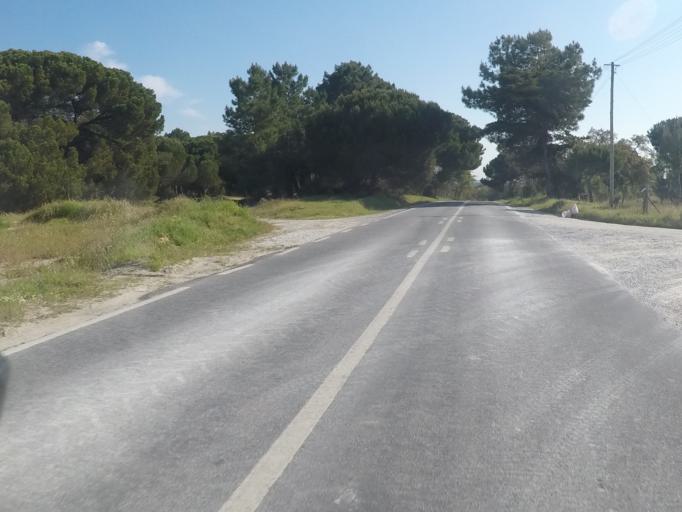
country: PT
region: Setubal
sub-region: Sesimbra
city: Sesimbra
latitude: 38.4949
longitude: -9.1546
